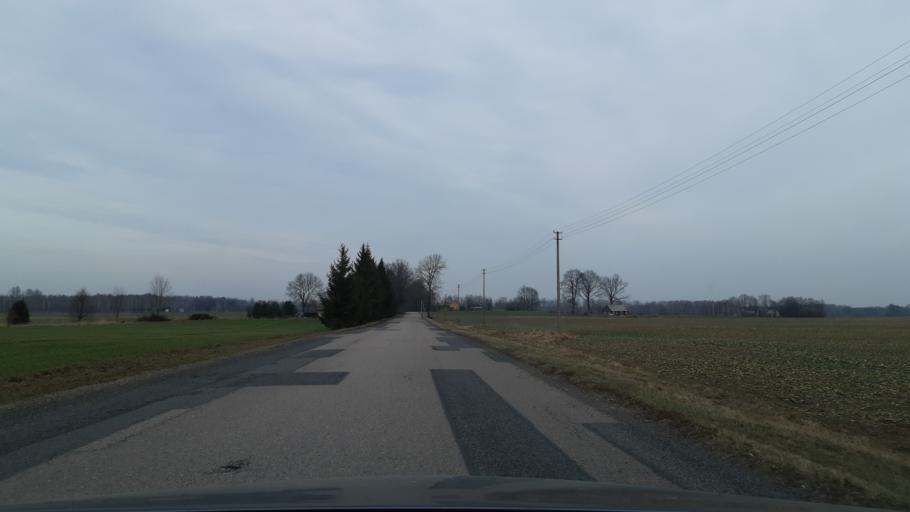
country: LT
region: Marijampoles apskritis
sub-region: Marijampole Municipality
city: Marijampole
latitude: 54.7197
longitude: 23.3340
